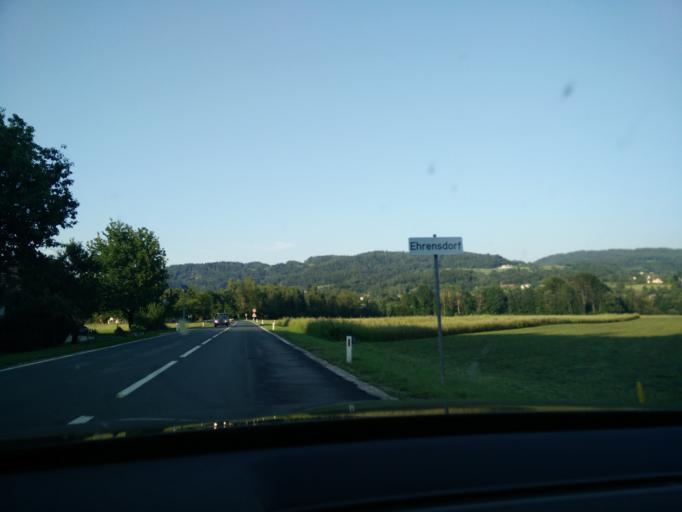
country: AT
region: Carinthia
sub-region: Politischer Bezirk Klagenfurt Land
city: Maria Rain
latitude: 46.5573
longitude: 14.2794
